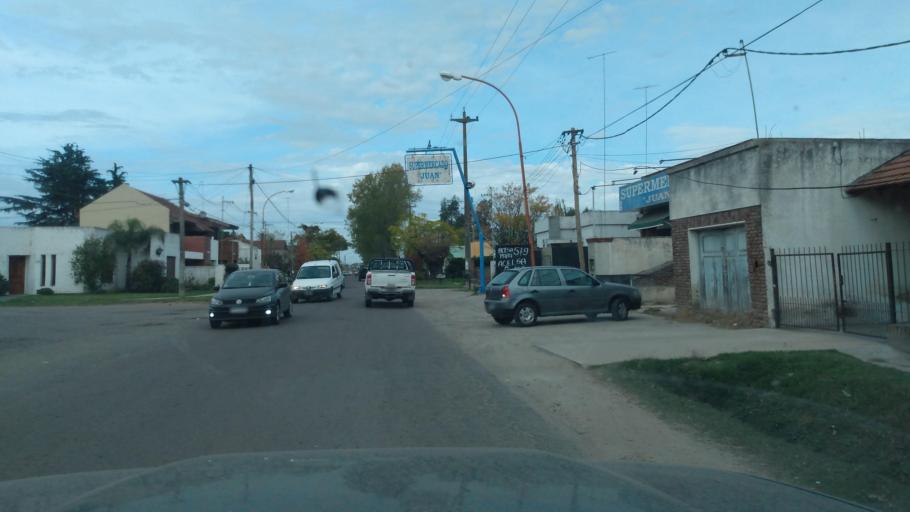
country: AR
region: Buenos Aires
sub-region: Partido de Lujan
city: Lujan
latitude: -34.6022
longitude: -59.1763
